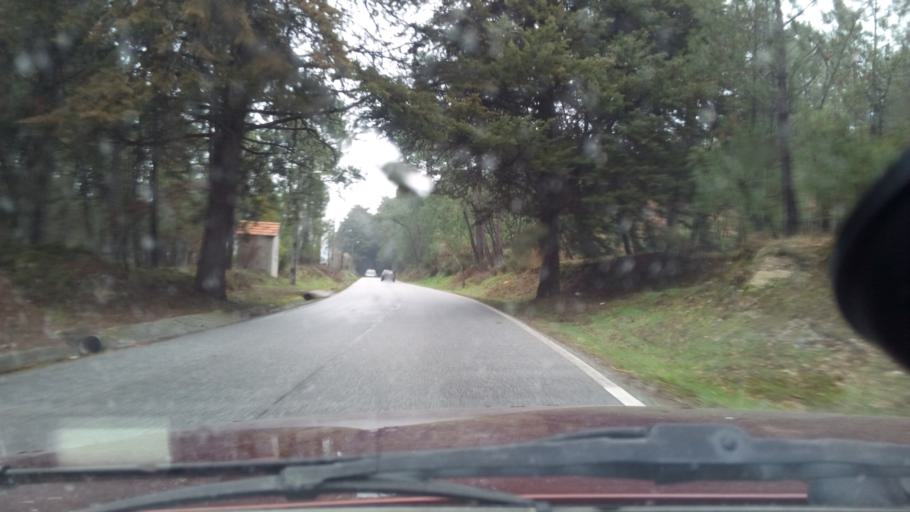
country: PT
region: Guarda
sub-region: Fornos de Algodres
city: Fornos de Algodres
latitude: 40.6092
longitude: -7.6271
